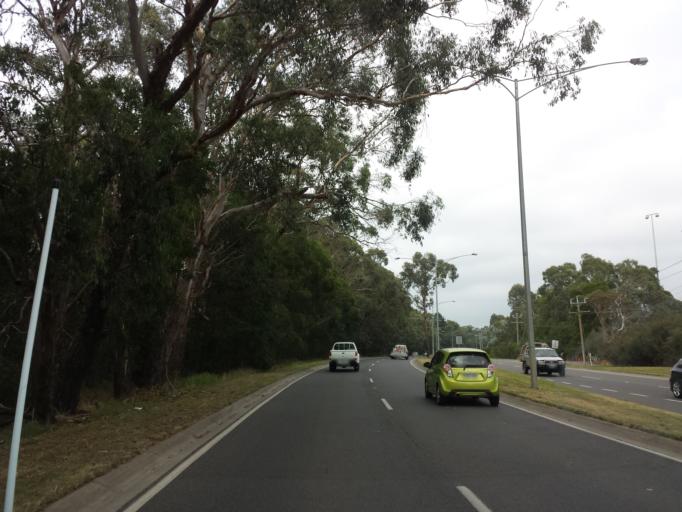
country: AU
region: Victoria
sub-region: Yarra Ranges
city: Montrose
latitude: -37.8022
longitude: 145.3581
